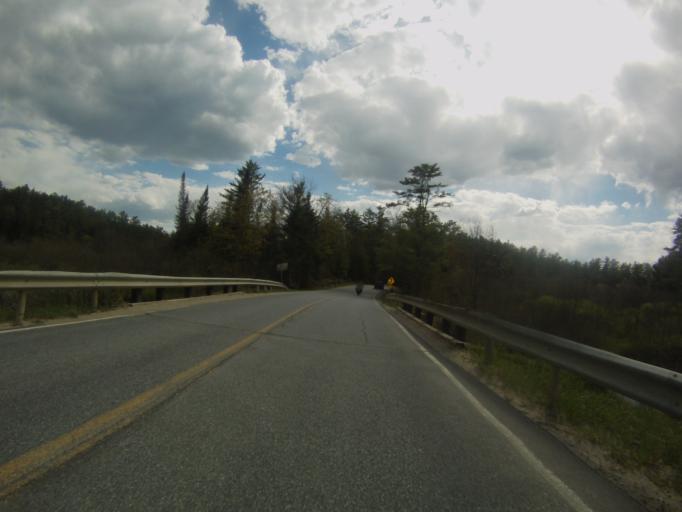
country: US
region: New York
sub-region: Essex County
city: Mineville
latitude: 43.9937
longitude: -73.6595
